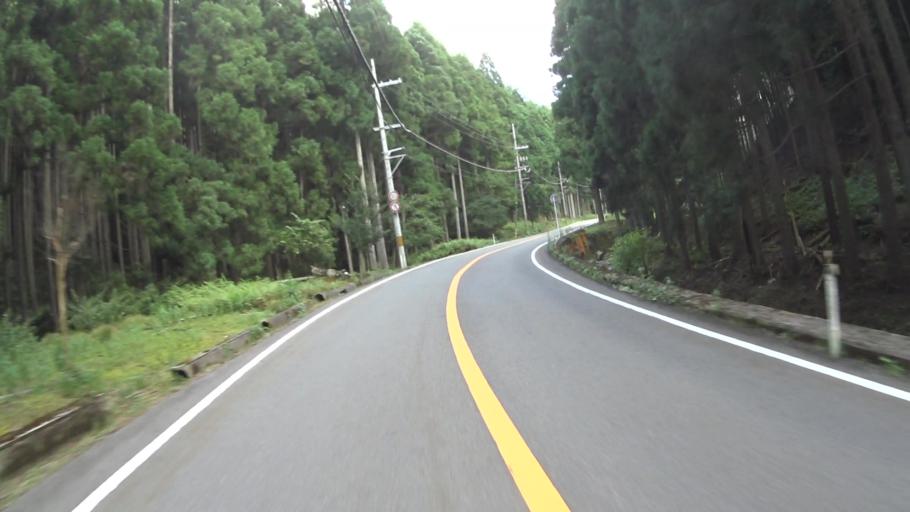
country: JP
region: Kyoto
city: Kameoka
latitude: 35.2597
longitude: 135.6117
